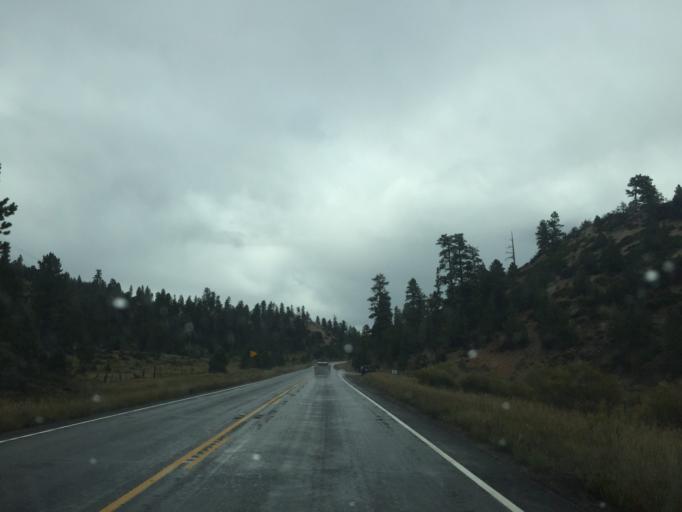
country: US
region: Utah
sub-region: Garfield County
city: Panguitch
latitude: 37.4655
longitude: -112.5181
